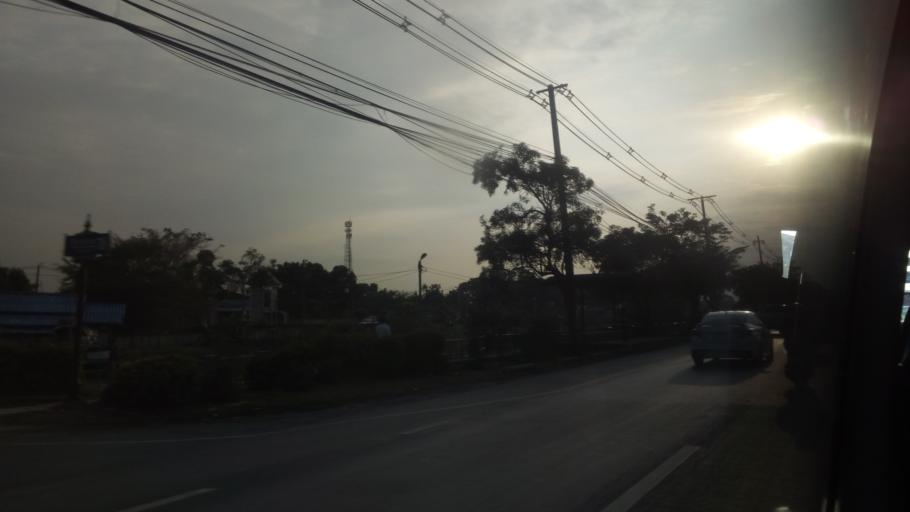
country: TH
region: Pathum Thani
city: Thanyaburi
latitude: 14.0023
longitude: 100.6927
